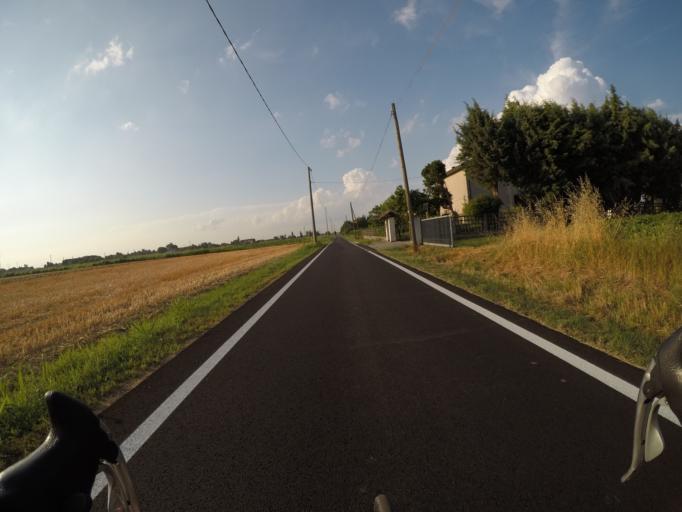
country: IT
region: Veneto
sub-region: Provincia di Rovigo
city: San Bellino
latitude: 45.0404
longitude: 11.5899
